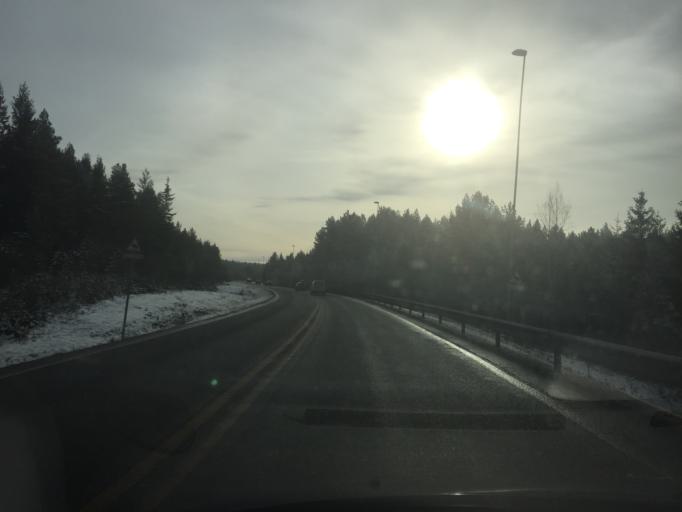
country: NO
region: Hedmark
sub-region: Loten
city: Loten
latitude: 60.7762
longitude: 11.3056
